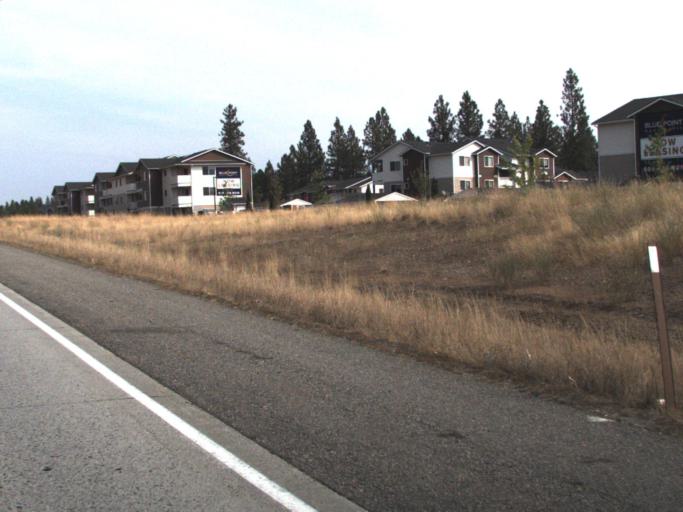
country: US
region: Washington
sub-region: Spokane County
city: Fairwood
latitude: 47.7947
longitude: -117.4076
